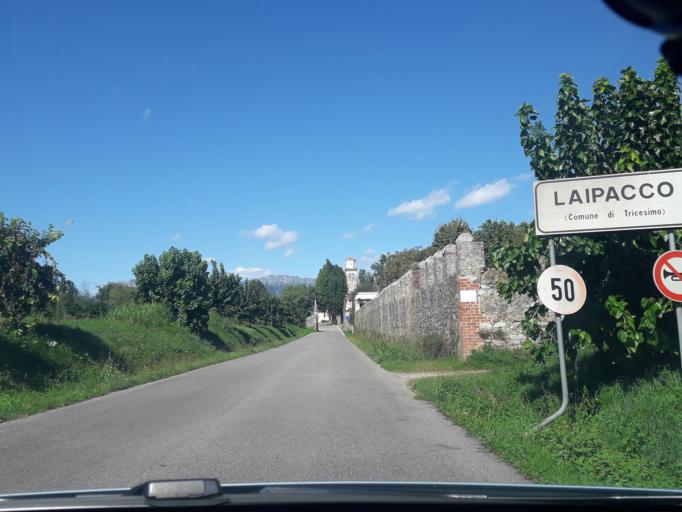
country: IT
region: Friuli Venezia Giulia
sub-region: Provincia di Udine
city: Reana del Roiale
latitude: 46.1475
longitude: 13.2154
